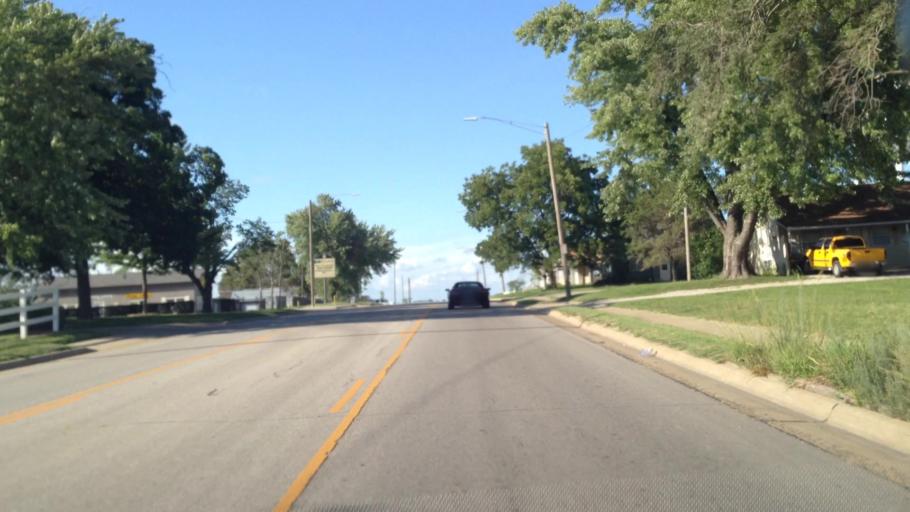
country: US
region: Kansas
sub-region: Franklin County
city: Ottawa
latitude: 38.6313
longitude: -95.2677
